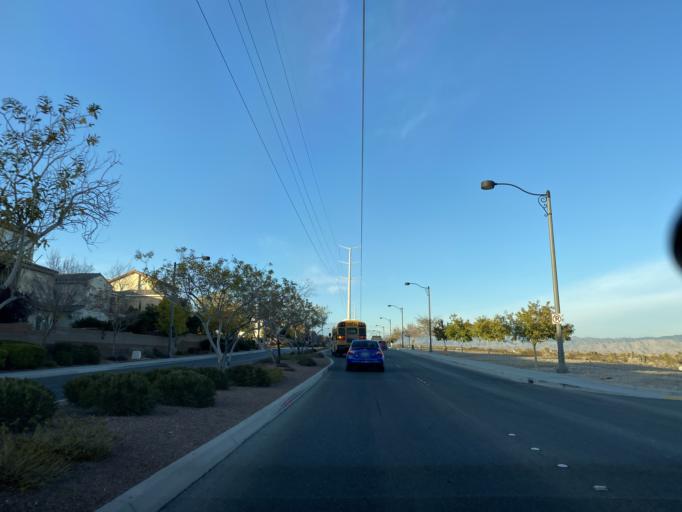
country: US
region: Nevada
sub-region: Clark County
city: Summerlin South
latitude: 36.2808
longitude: -115.3288
